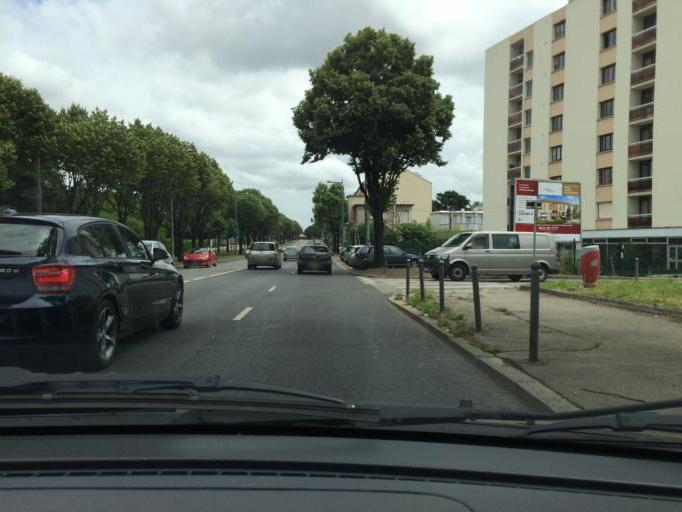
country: FR
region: Rhone-Alpes
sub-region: Departement du Rhone
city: Bron
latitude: 45.7377
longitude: 4.8961
